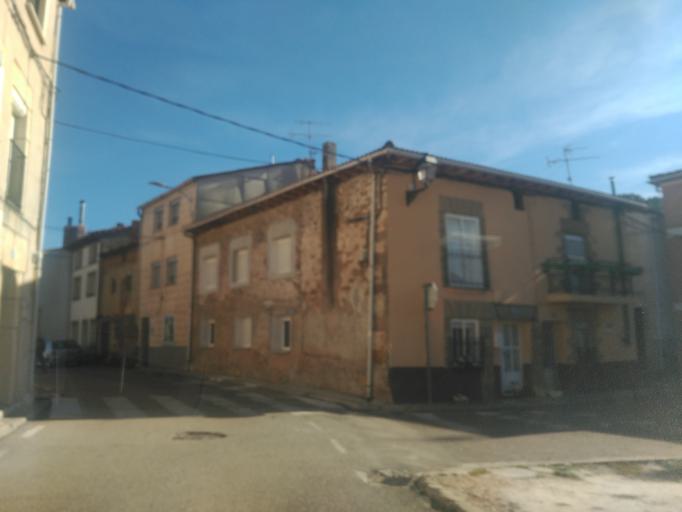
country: ES
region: Castille and Leon
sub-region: Provincia de Soria
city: Espejon
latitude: 41.8303
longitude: -3.2579
